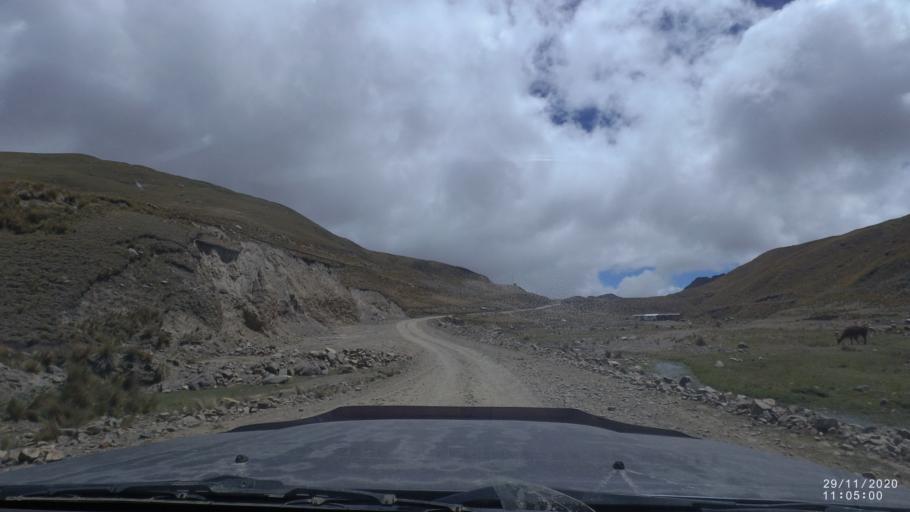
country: BO
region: Cochabamba
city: Cochabamba
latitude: -17.1884
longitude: -66.2133
